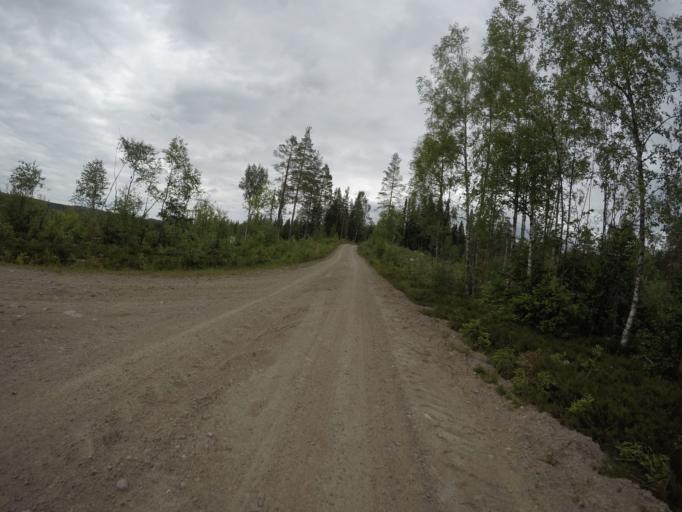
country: SE
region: Dalarna
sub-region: Ludvika Kommun
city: Abborrberget
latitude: 60.0835
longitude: 14.5541
